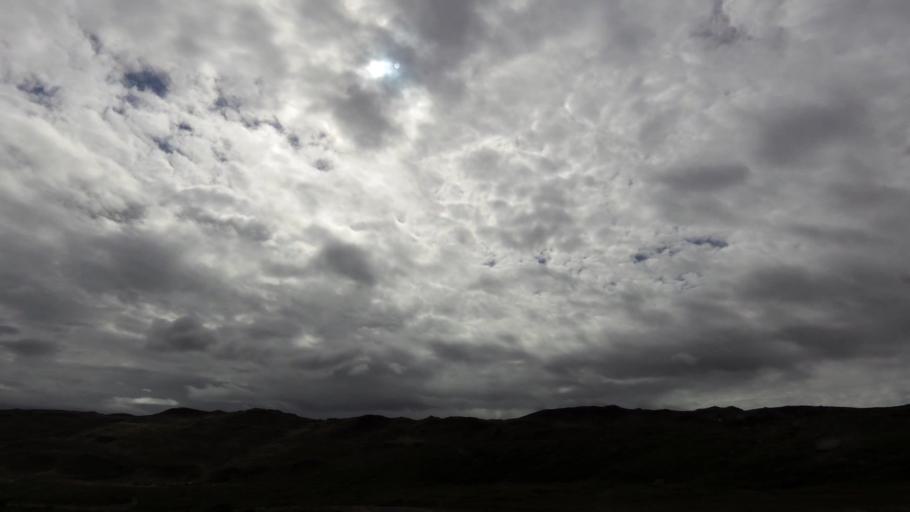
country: IS
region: West
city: Stykkisholmur
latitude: 65.5379
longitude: -22.1195
